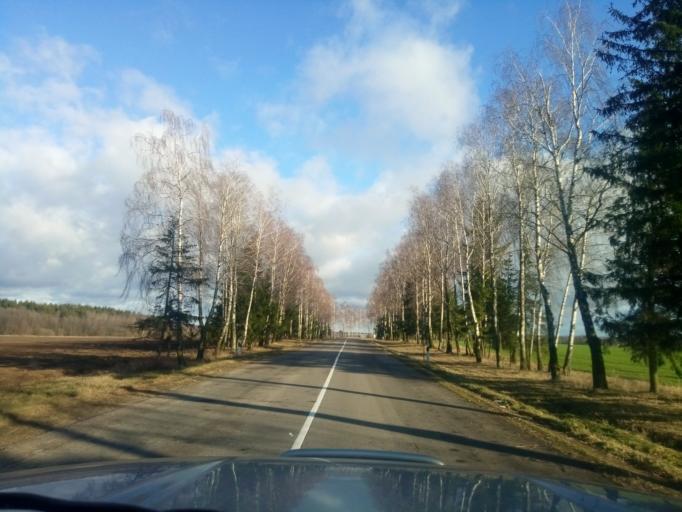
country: BY
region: Minsk
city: Tsimkavichy
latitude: 53.1748
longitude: 26.9409
